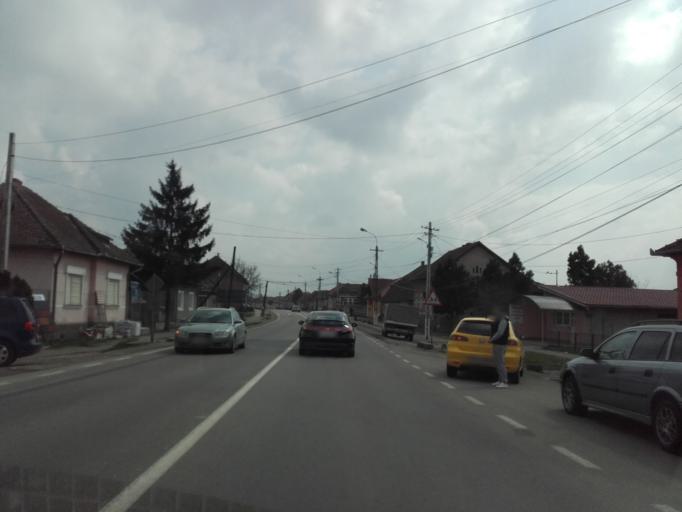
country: RO
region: Mures
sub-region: Comuna Iernut
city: Iernut
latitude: 46.4500
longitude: 24.2360
